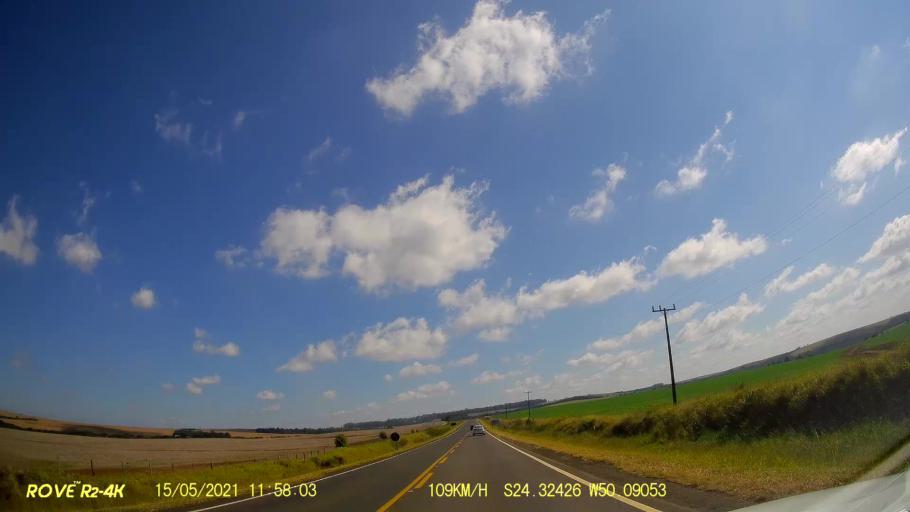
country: BR
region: Parana
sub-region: Pirai Do Sul
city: Pirai do Sul
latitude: -24.3238
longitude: -50.0912
